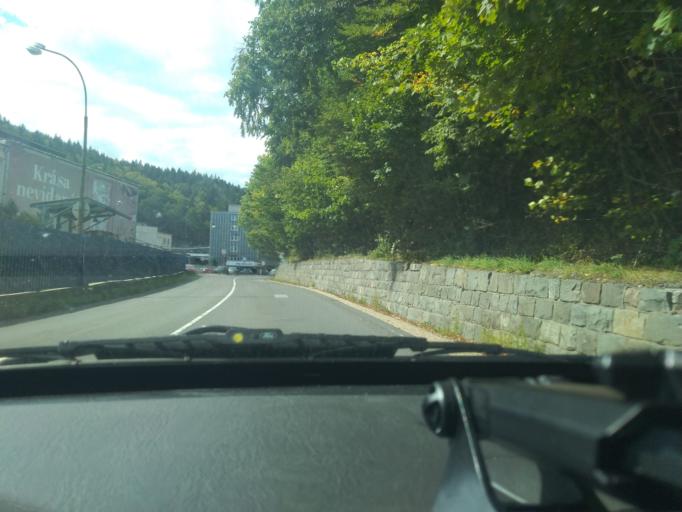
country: SK
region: Banskobystricky
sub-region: Okres Banska Bystrica
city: Banska Bystrica
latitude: 48.7943
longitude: 19.0836
